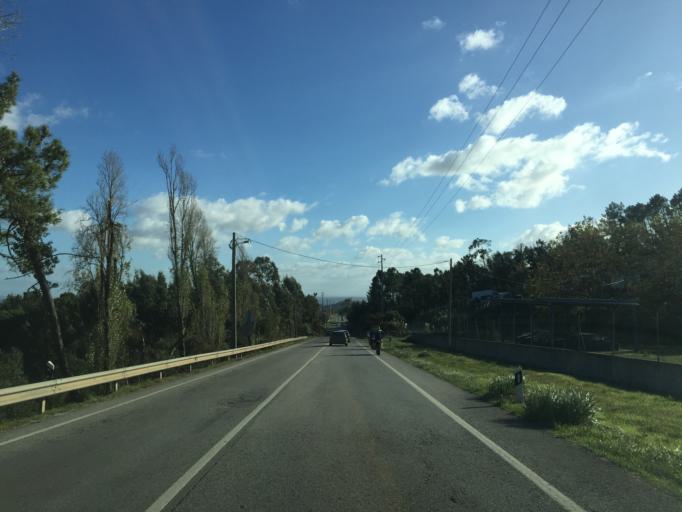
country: PT
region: Coimbra
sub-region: Figueira da Foz
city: Tavarede
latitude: 40.1855
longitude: -8.8295
